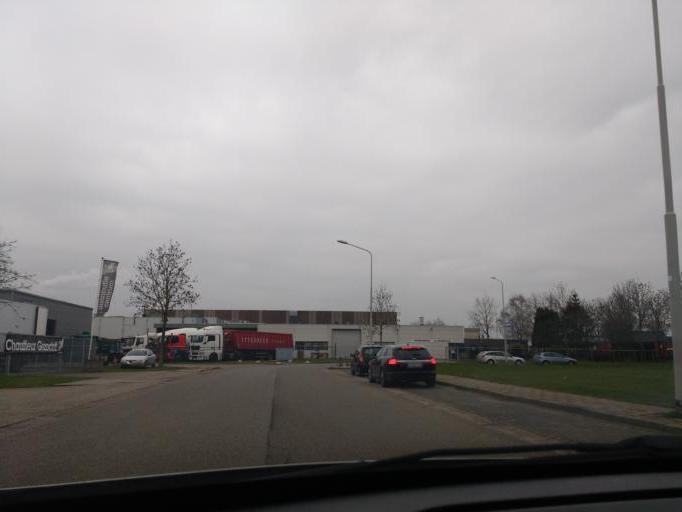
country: NL
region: Gelderland
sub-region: Gemeente Nijmegen
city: Lindenholt
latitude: 51.8428
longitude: 5.8066
